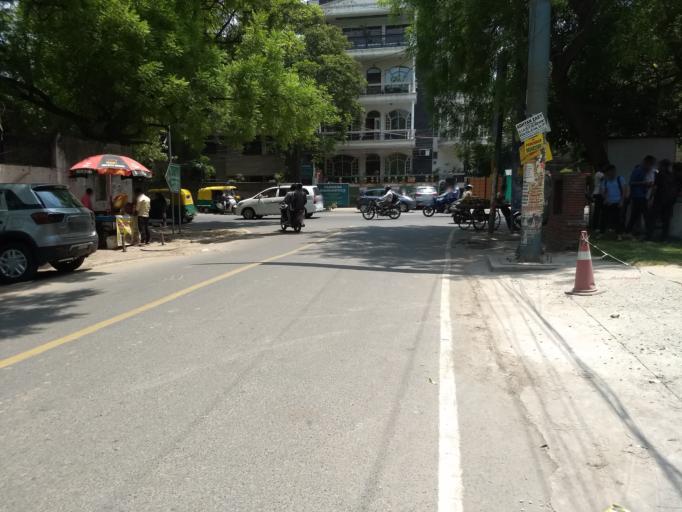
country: IN
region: NCT
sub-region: New Delhi
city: New Delhi
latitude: 28.5328
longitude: 77.2038
